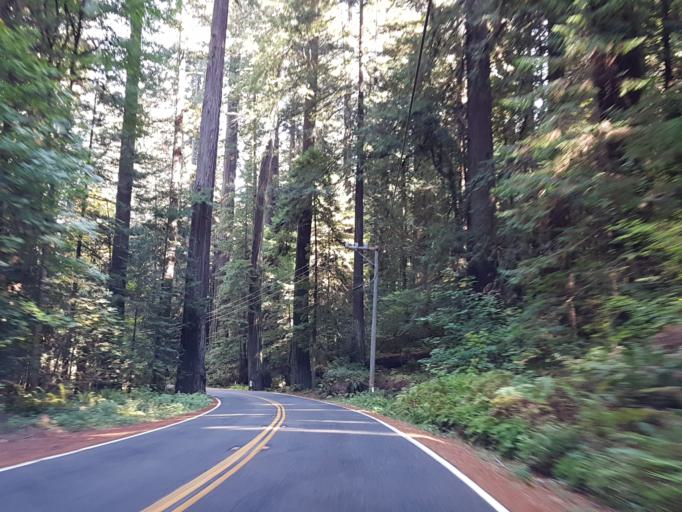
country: US
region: California
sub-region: Humboldt County
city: Rio Dell
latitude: 40.4162
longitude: -123.9707
